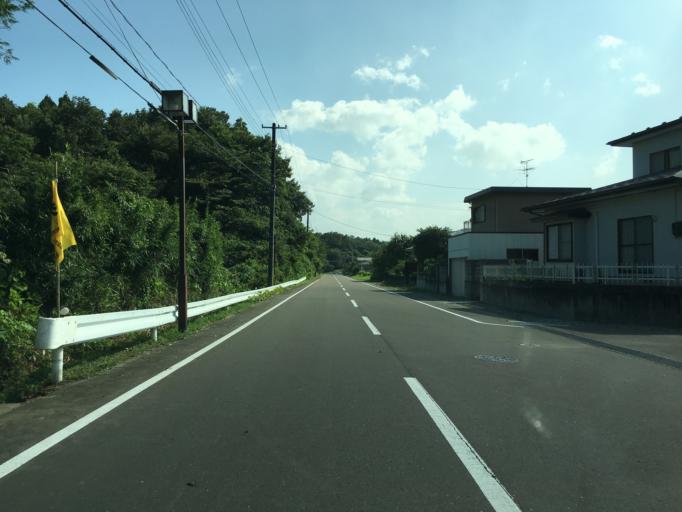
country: JP
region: Miyagi
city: Marumori
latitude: 37.9428
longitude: 140.7728
